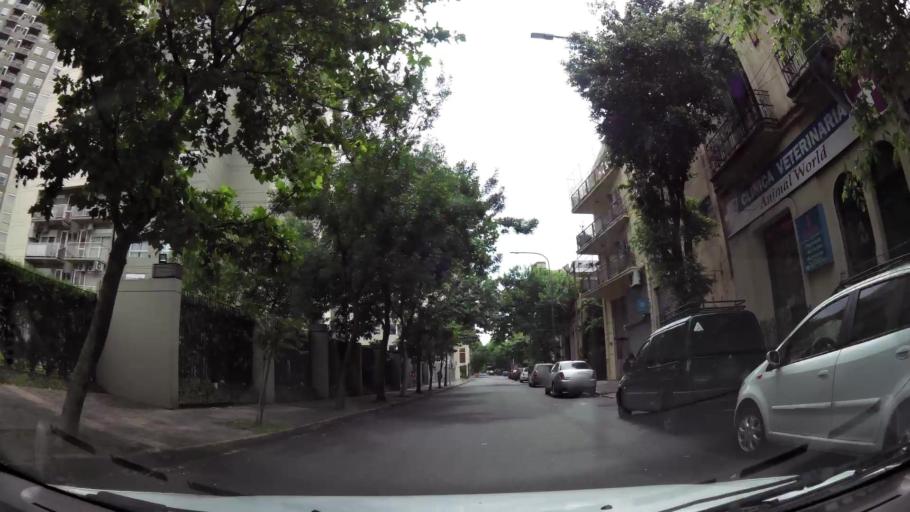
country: AR
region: Buenos Aires F.D.
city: Retiro
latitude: -34.6016
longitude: -58.4130
